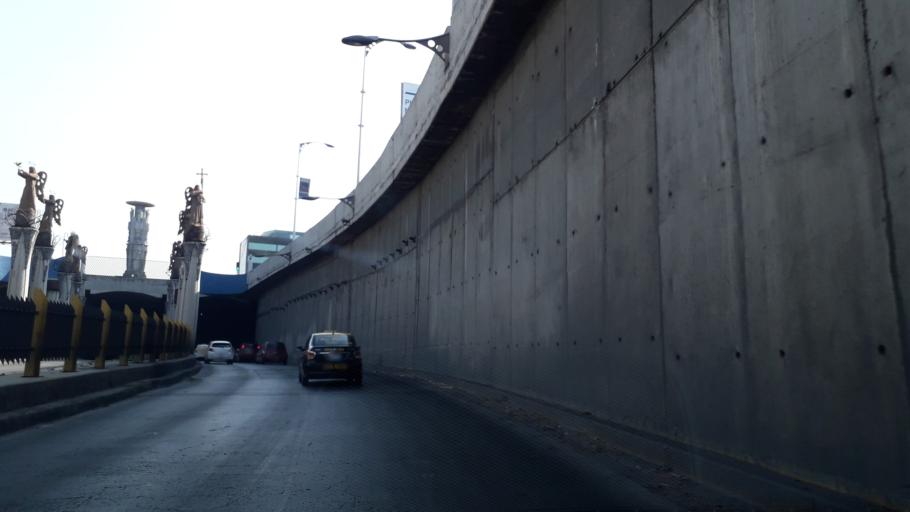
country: MX
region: Puebla
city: Puebla
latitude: 19.0528
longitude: -98.2232
